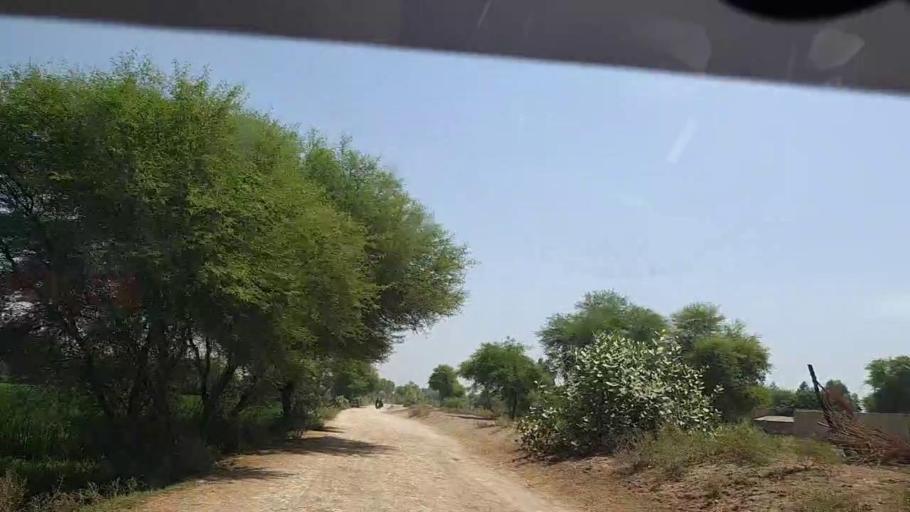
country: PK
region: Sindh
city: Ghauspur
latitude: 28.1690
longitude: 69.1216
